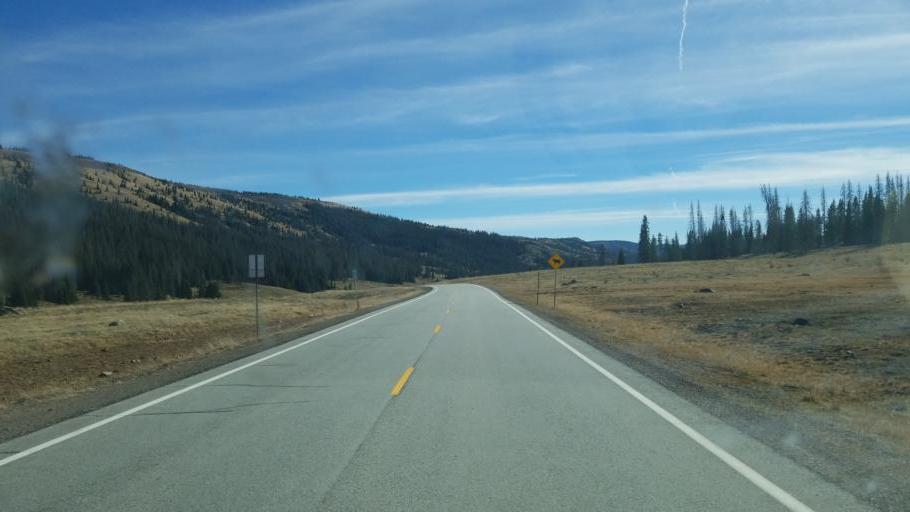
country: US
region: New Mexico
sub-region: Rio Arriba County
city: Chama
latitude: 37.0654
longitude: -106.3965
